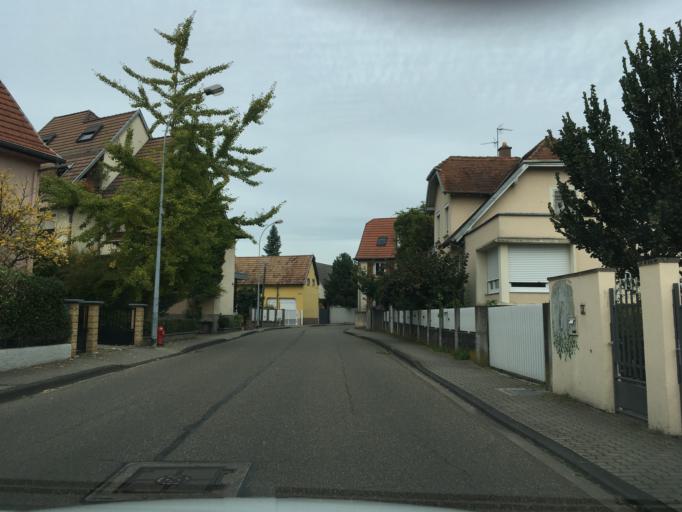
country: FR
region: Alsace
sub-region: Departement du Bas-Rhin
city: Bischheim
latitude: 48.6068
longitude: 7.7886
